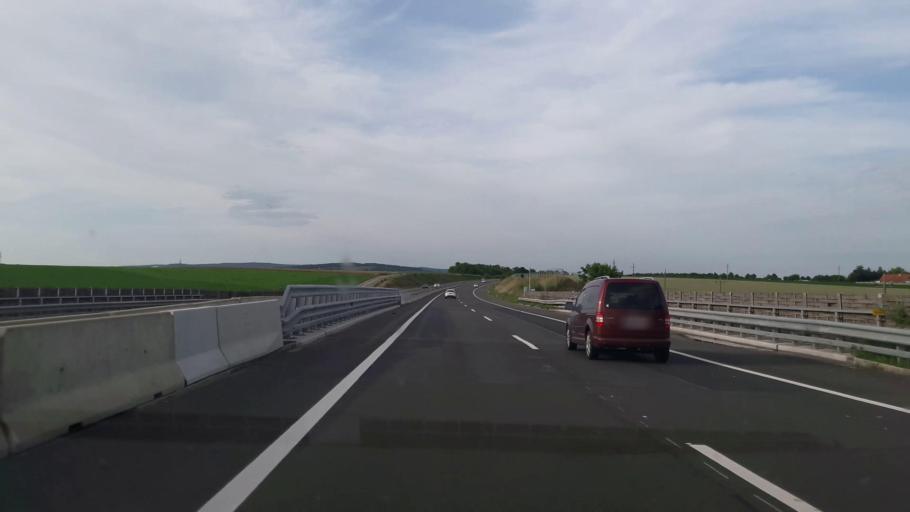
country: AT
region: Burgenland
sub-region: Politischer Bezirk Mattersburg
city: Hirm
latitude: 47.7874
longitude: 16.4420
